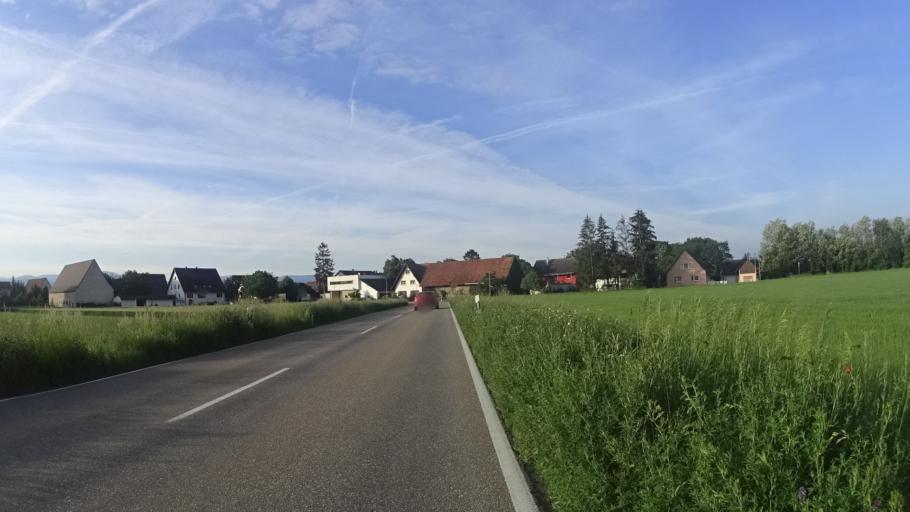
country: DE
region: Baden-Wuerttemberg
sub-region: Freiburg Region
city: Hartheim
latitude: 47.9688
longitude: 7.6439
